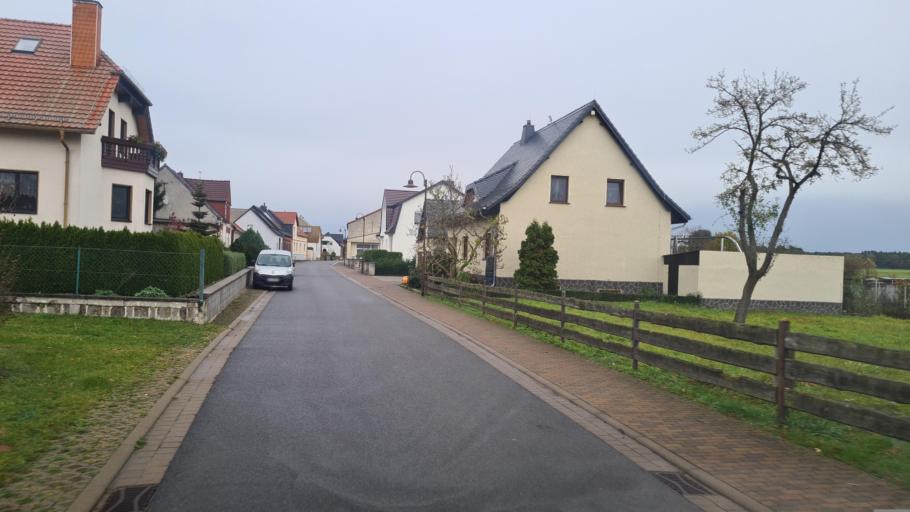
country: DE
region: Saxony-Anhalt
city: Abtsdorf
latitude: 51.9301
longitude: 12.6772
